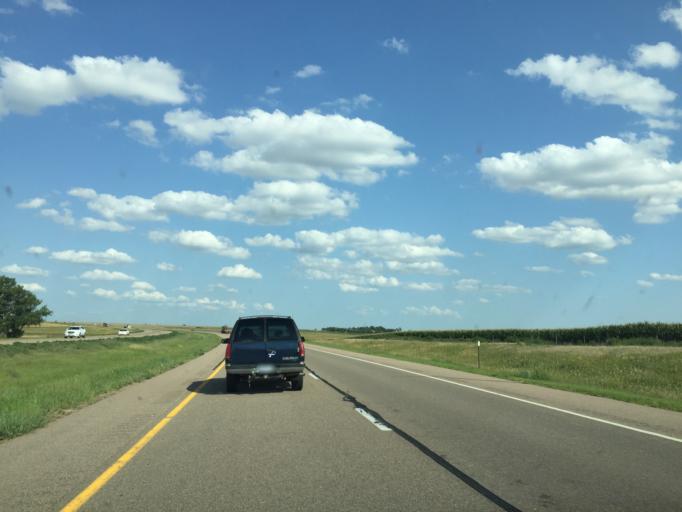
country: US
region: Kansas
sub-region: Trego County
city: WaKeeney
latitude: 39.0255
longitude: -100.1727
